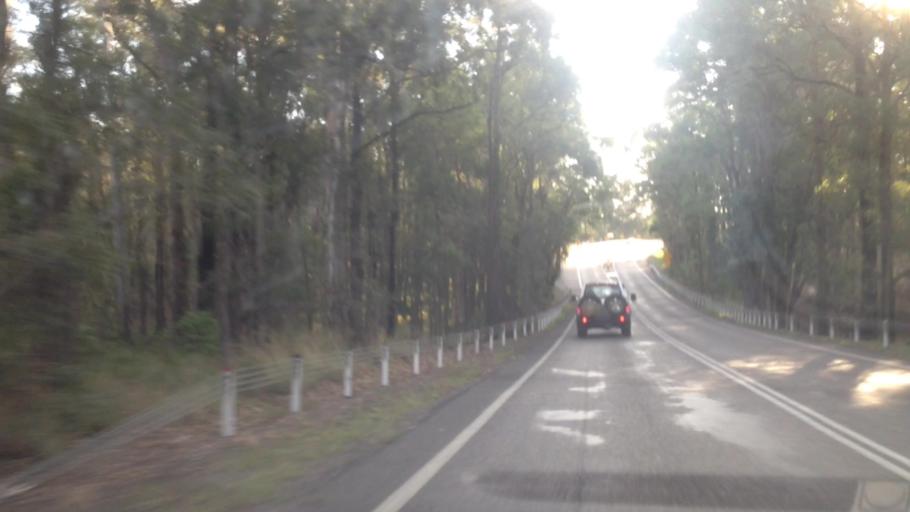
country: AU
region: New South Wales
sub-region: Cessnock
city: Heddon Greta
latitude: -32.8304
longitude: 151.5116
